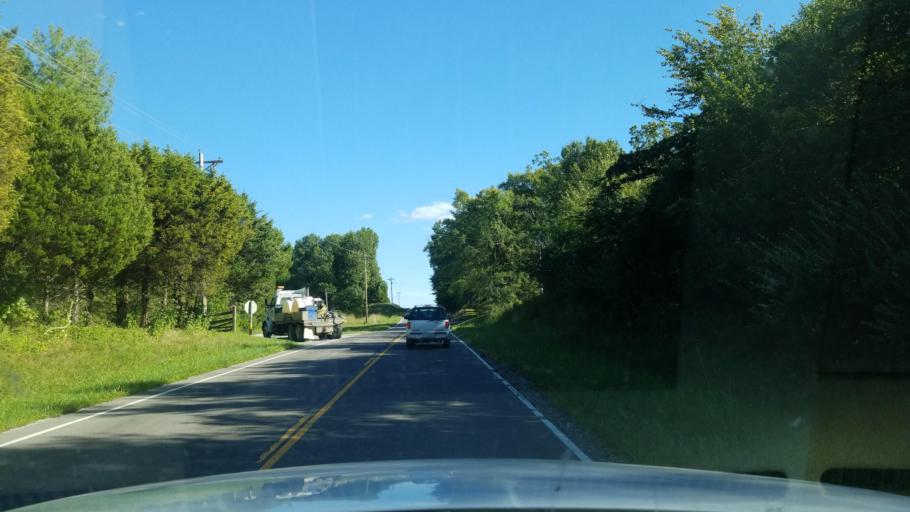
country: US
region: Illinois
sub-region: Saline County
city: Harrisburg
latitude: 37.6233
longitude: -88.4733
